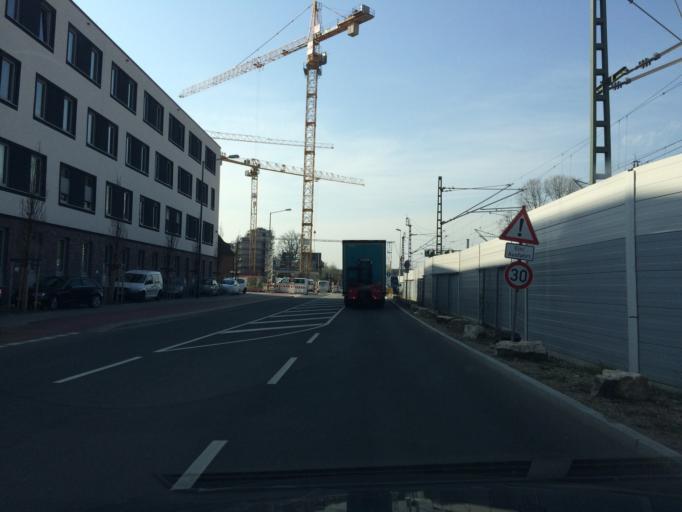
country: DE
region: Bavaria
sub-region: Regierungsbezirk Mittelfranken
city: Erlangen
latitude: 49.5917
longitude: 11.0027
